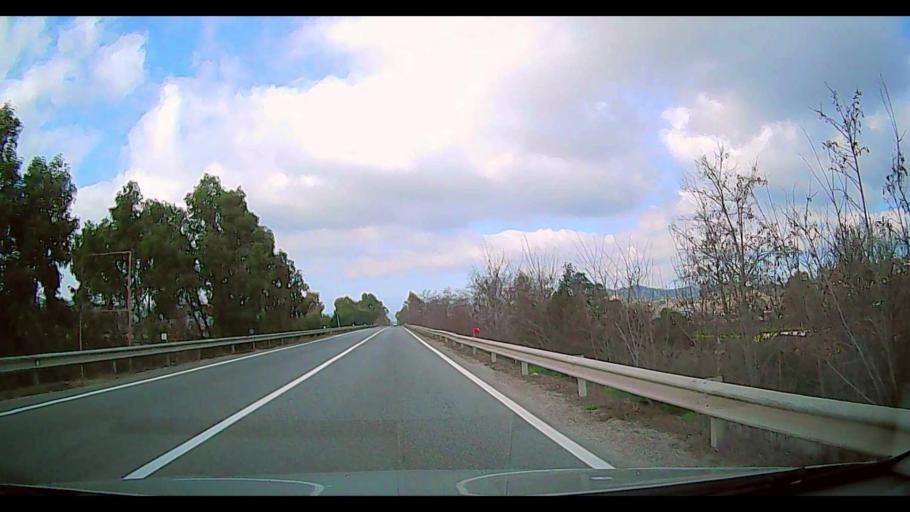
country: IT
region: Calabria
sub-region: Provincia di Crotone
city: Rocca di Neto
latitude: 39.1761
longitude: 17.0124
